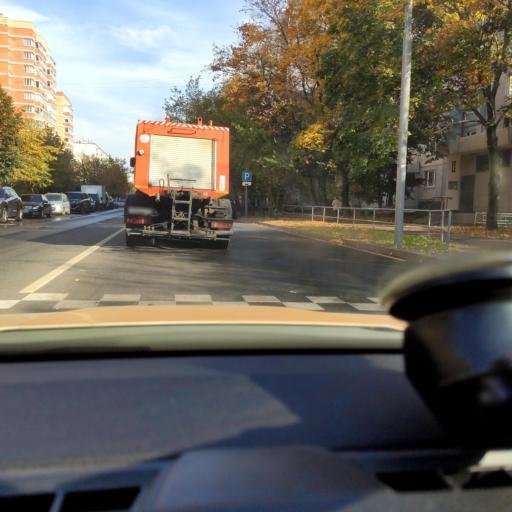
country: RU
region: Moscow
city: Ivanovskoye
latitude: 55.7772
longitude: 37.8269
